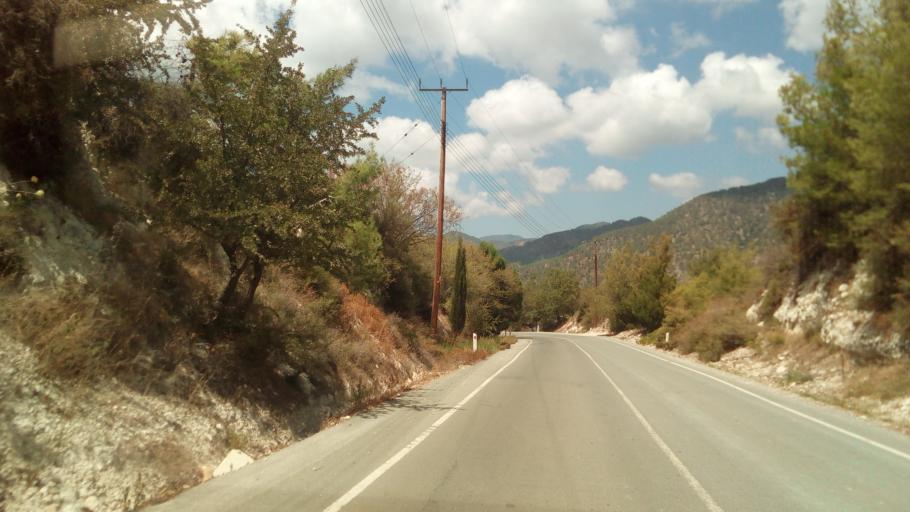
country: CY
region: Pafos
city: Mesogi
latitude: 34.9280
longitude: 32.6226
